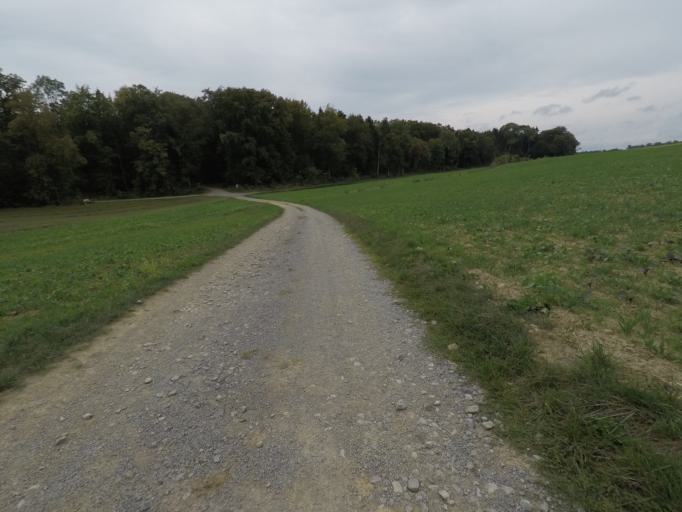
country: DE
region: Baden-Wuerttemberg
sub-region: Regierungsbezirk Stuttgart
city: Herrenberg
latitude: 48.6014
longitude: 8.8220
